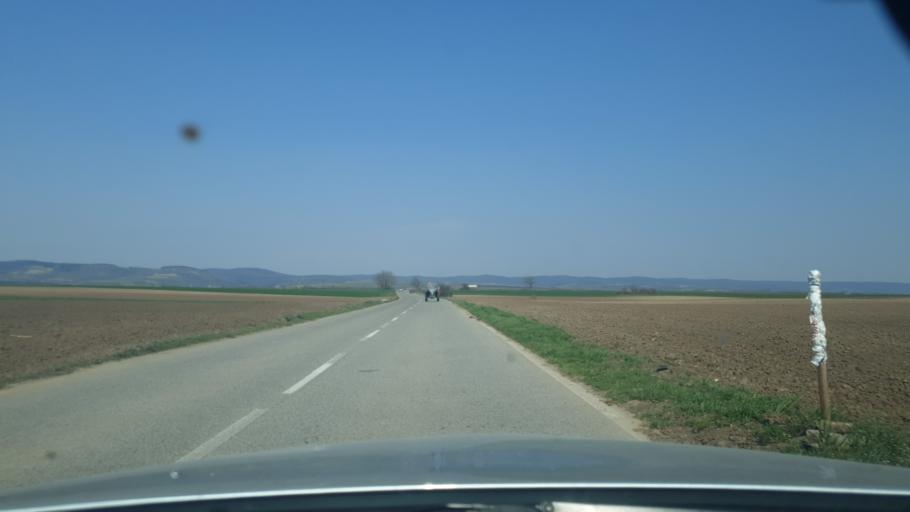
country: RS
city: Vrdnik
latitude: 45.0602
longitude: 19.7680
